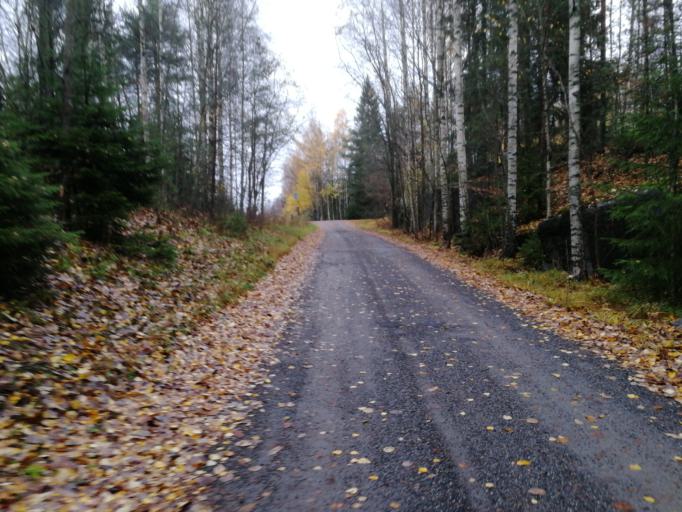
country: FI
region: Pirkanmaa
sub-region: Tampere
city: Tampere
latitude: 61.4566
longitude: 23.8703
